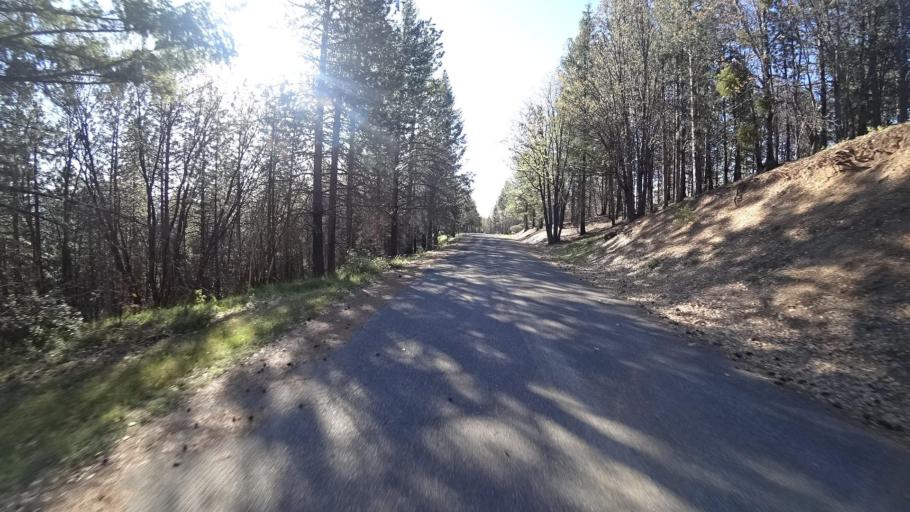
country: US
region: California
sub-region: Lake County
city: Upper Lake
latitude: 39.3129
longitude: -122.9451
